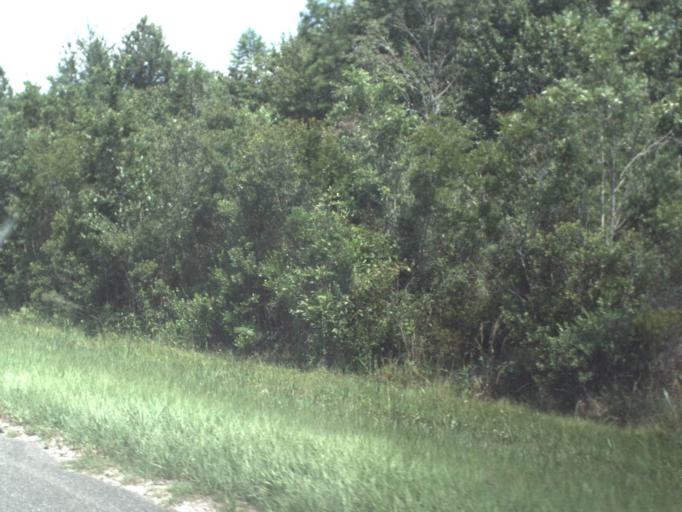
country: US
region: Florida
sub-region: Baker County
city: Macclenny
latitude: 30.2706
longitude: -82.1890
